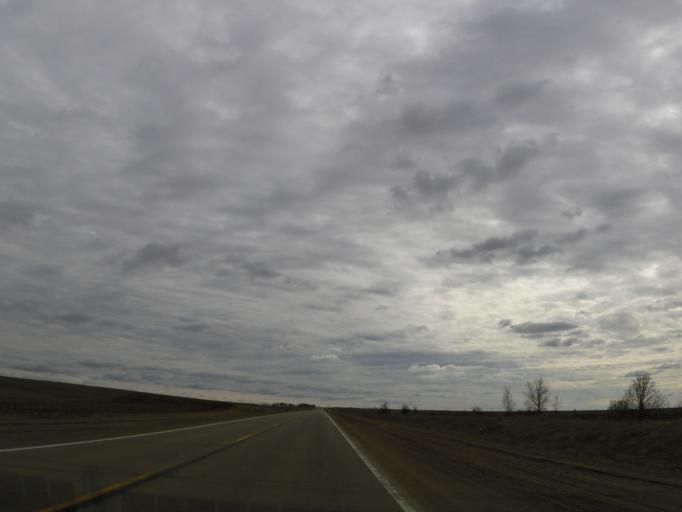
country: US
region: Iowa
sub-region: Howard County
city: Cresco
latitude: 43.4381
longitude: -92.2985
